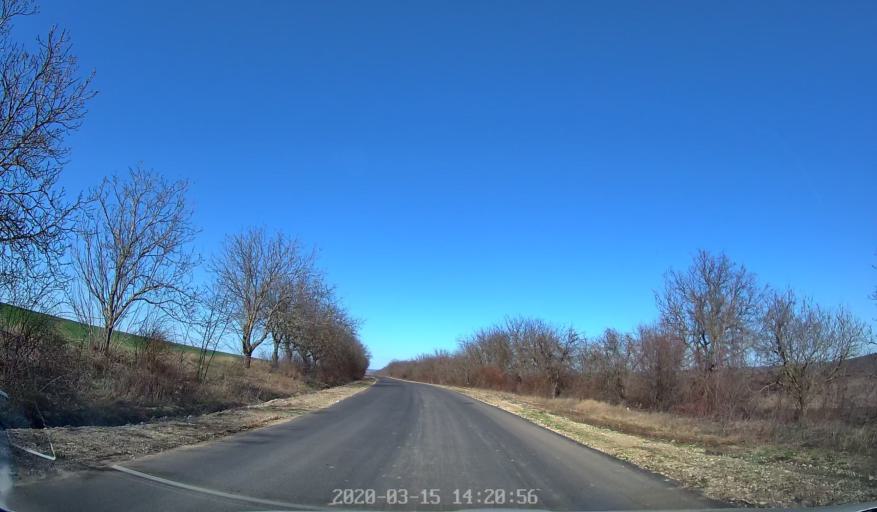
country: MD
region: Orhei
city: Orhei
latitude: 47.3128
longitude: 28.9246
